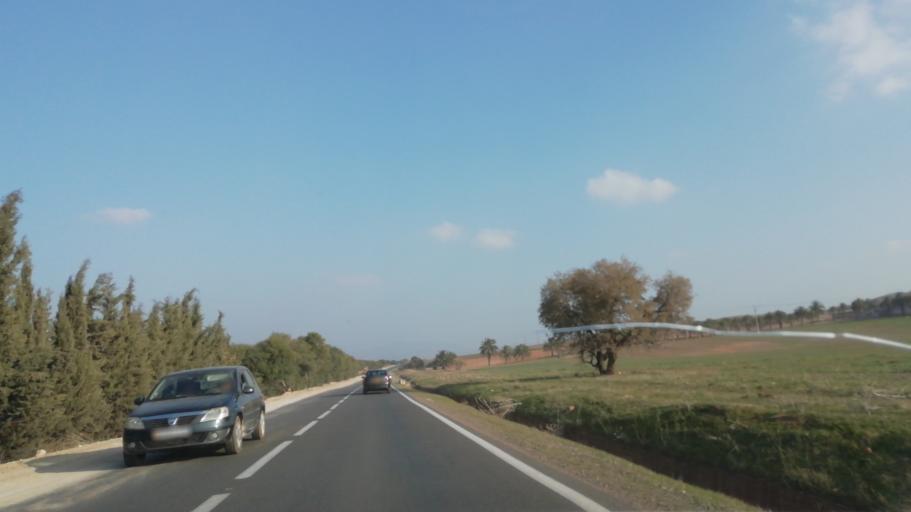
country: DZ
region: Ain Temouchent
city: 'Ain Temouchent
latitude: 35.3052
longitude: -1.0515
